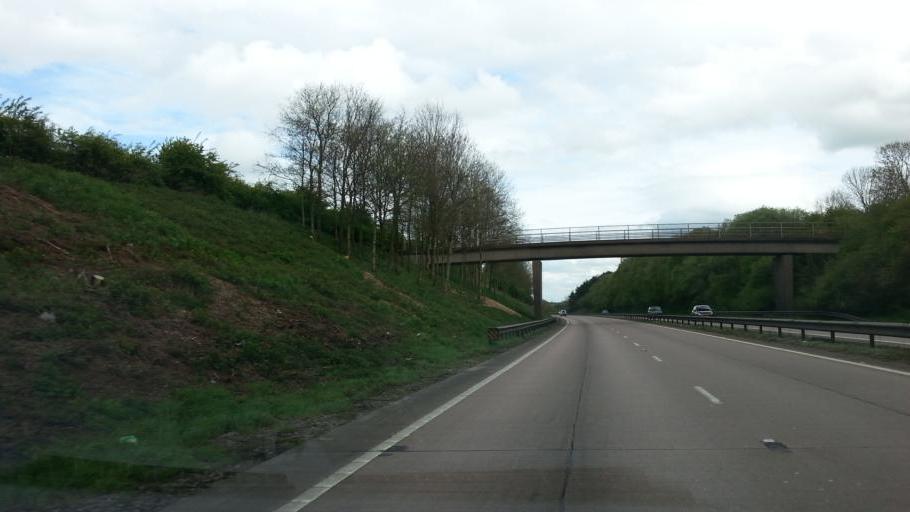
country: GB
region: England
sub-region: Staffordshire
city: Cheadle
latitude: 52.9559
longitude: -2.0409
